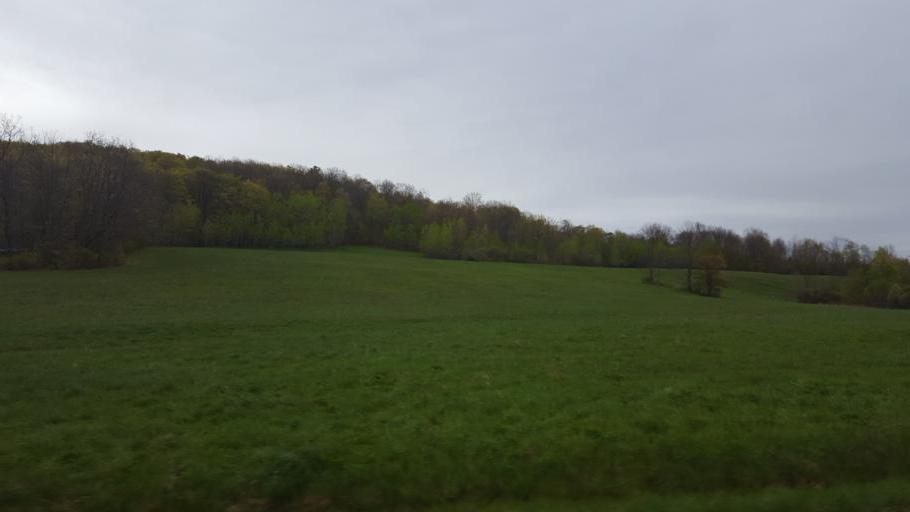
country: US
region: Pennsylvania
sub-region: Tioga County
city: Westfield
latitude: 42.0398
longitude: -77.4664
